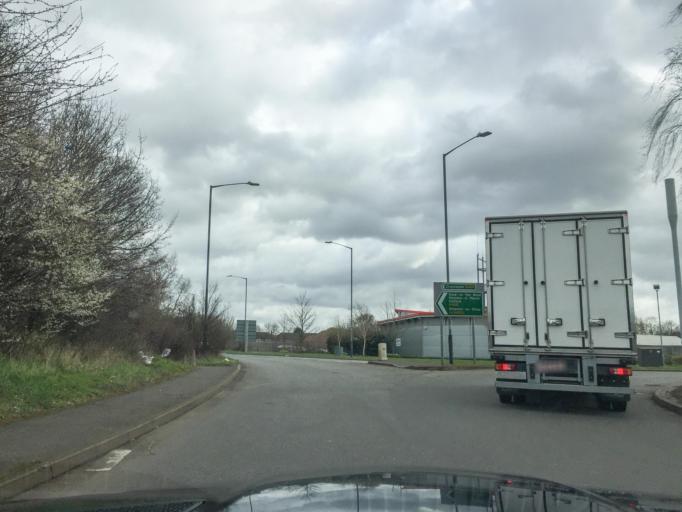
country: GB
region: England
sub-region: Warwickshire
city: Wellesbourne Mountford
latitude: 52.1922
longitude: -1.6039
